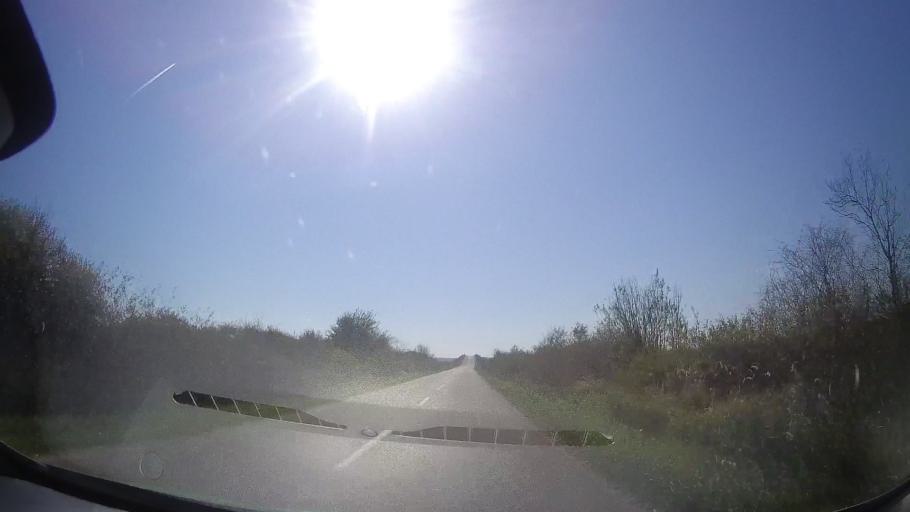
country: RO
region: Timis
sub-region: Comuna Bethausen
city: Bethausen
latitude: 45.8201
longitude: 21.9598
